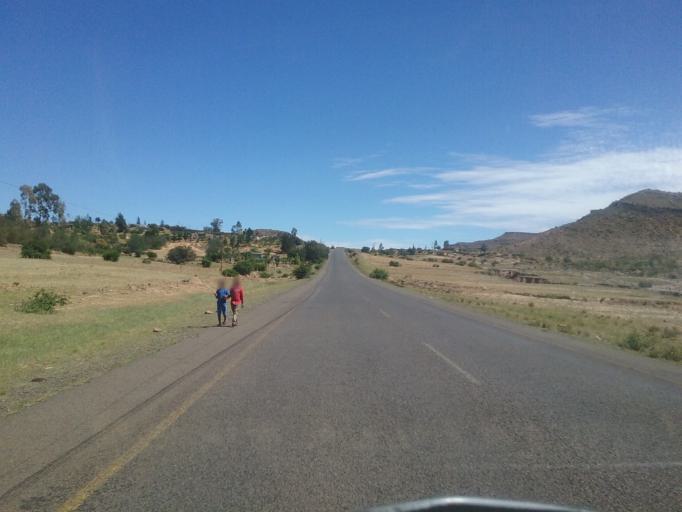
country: LS
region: Quthing
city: Quthing
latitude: -30.3607
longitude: 27.5483
